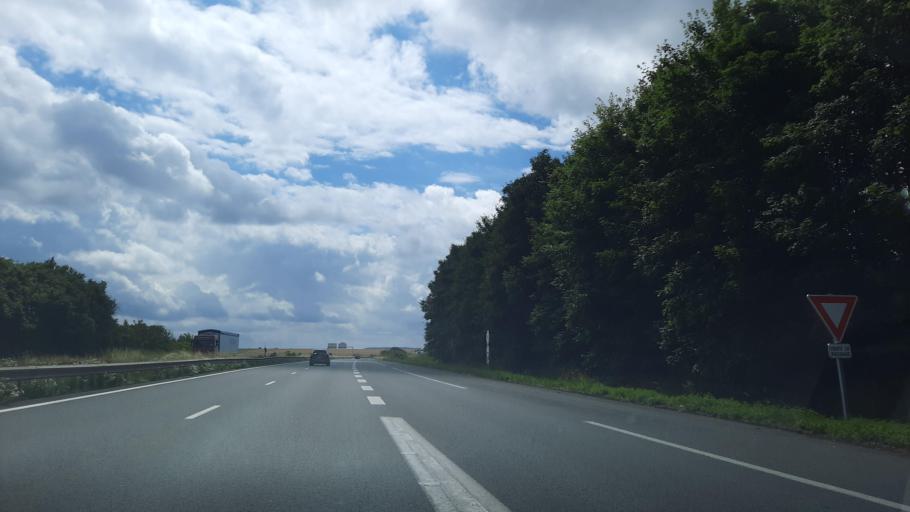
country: FR
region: Nord-Pas-de-Calais
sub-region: Departement du Nord
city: Marcoing
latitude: 50.1357
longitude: 3.1414
